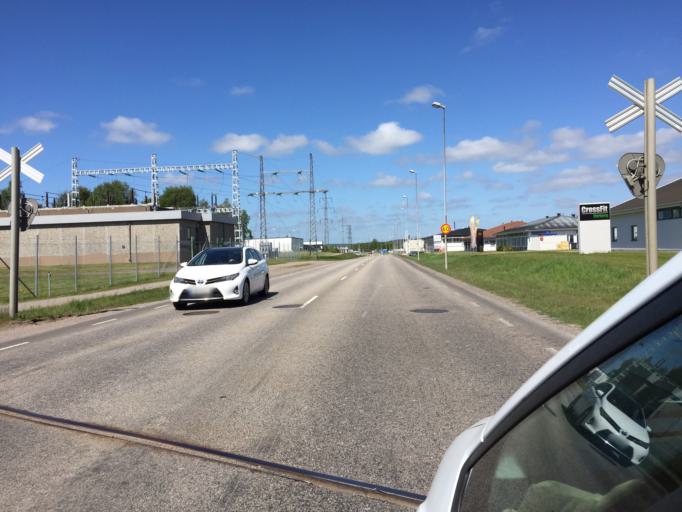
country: SE
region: Halland
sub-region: Varbergs Kommun
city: Varberg
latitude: 57.1189
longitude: 12.2895
